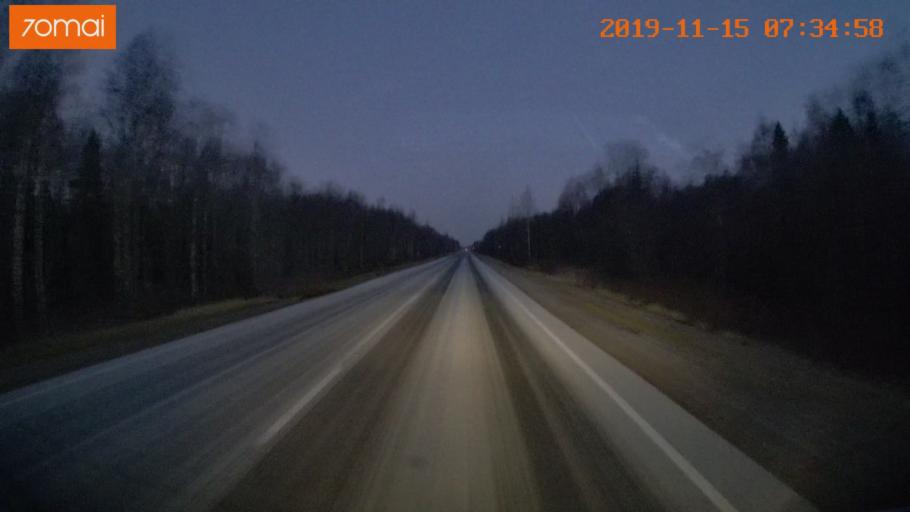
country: RU
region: Vologda
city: Sheksna
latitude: 58.7253
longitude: 38.4604
